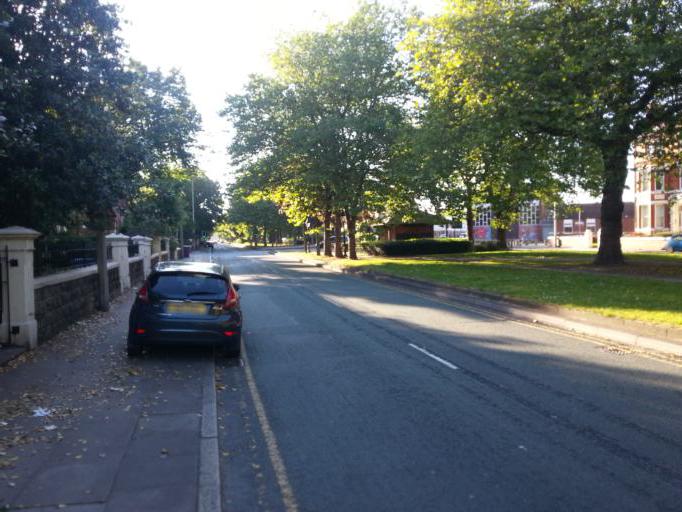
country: GB
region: England
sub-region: Liverpool
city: Liverpool
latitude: 53.3915
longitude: -2.9583
